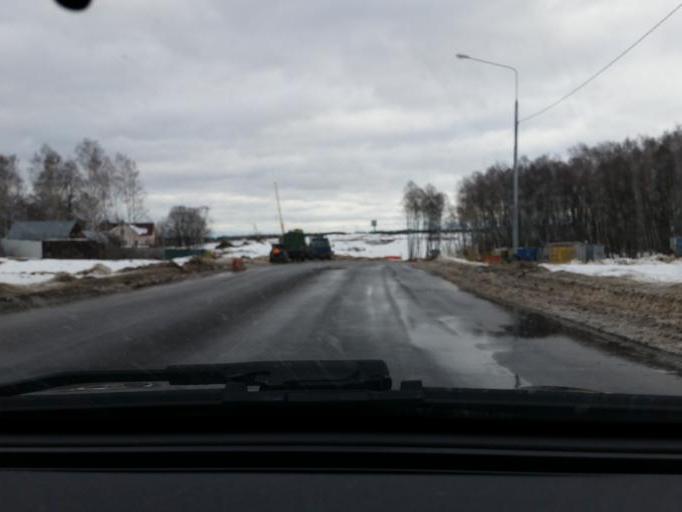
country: RU
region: Moskovskaya
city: Shcherbinka
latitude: 55.5256
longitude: 37.5994
